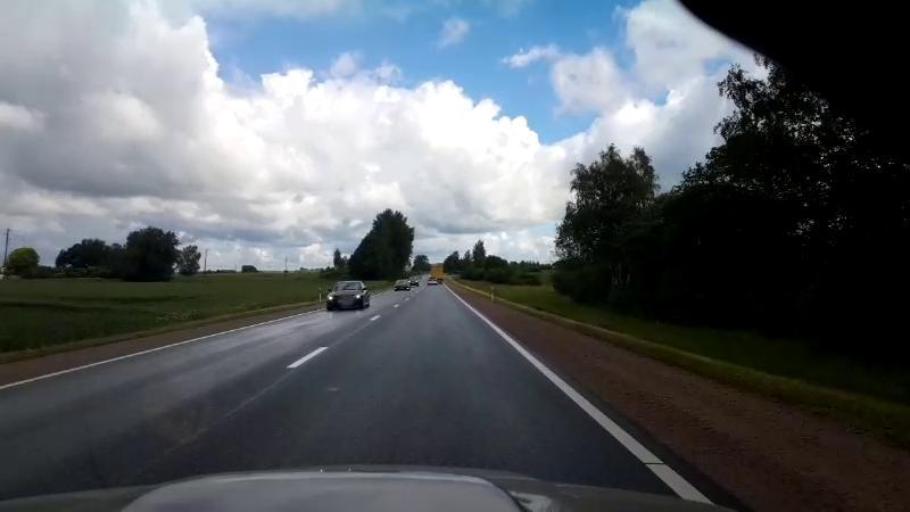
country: LV
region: Bauskas Rajons
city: Bauska
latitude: 56.4921
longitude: 24.1763
